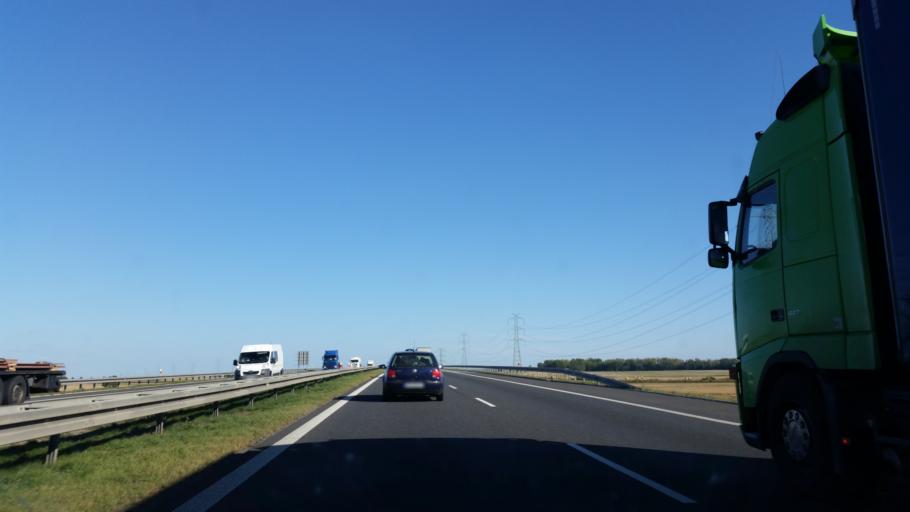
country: PL
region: Opole Voivodeship
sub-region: Powiat brzeski
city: Olszanka
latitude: 50.7506
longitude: 17.4419
